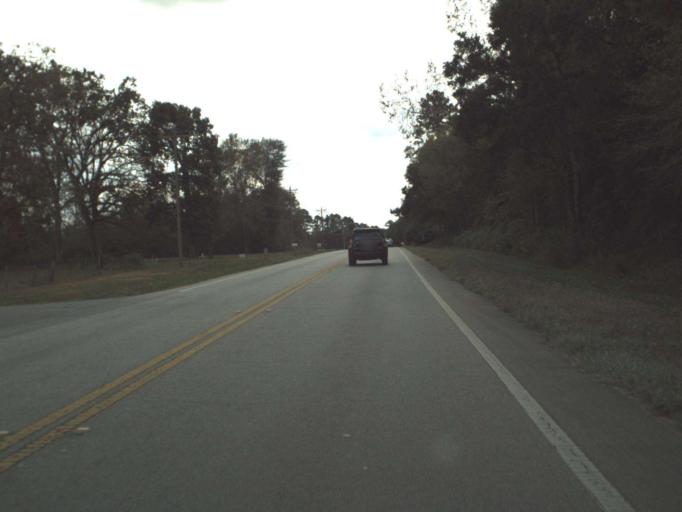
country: US
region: Florida
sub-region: Gadsden County
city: Quincy
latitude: 30.6485
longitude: -84.6010
